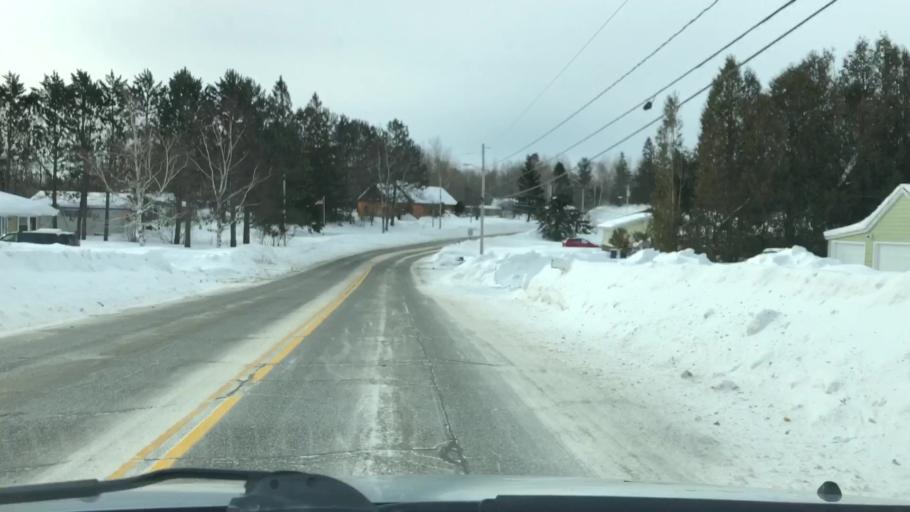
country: US
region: Minnesota
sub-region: Saint Louis County
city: Duluth
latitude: 46.7948
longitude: -92.1494
